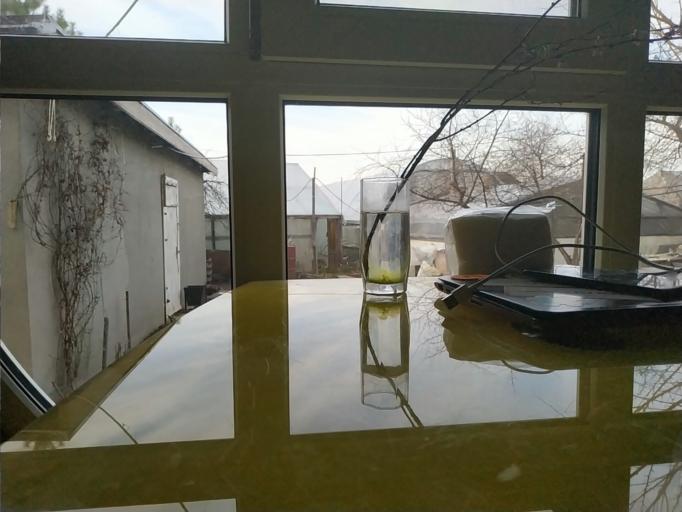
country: RU
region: Republic of Karelia
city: Suoyarvi
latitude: 61.8534
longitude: 32.2767
